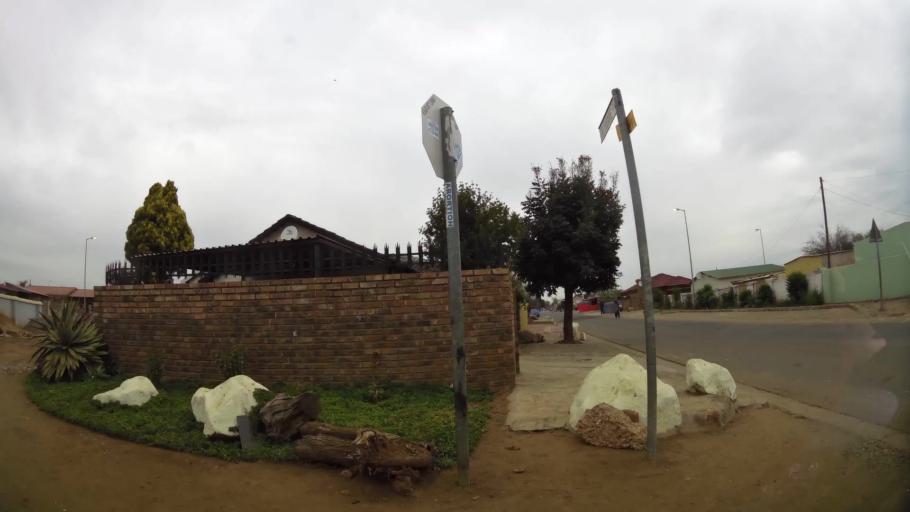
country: ZA
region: Gauteng
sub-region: City of Tshwane Metropolitan Municipality
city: Cullinan
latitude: -25.7062
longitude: 28.3570
